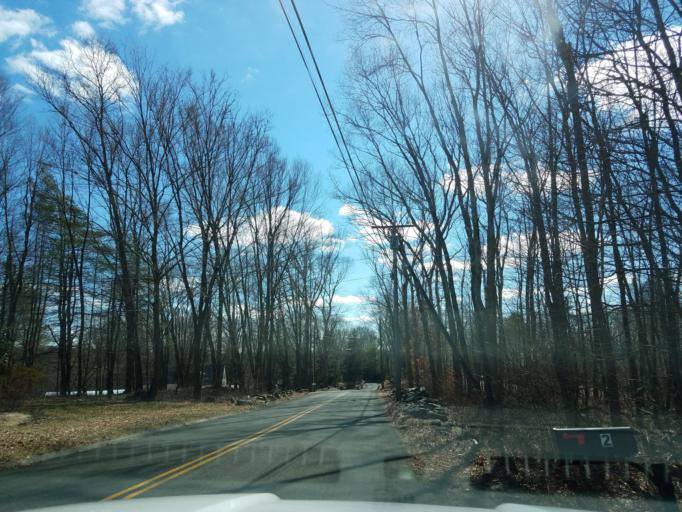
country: US
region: Connecticut
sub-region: Windham County
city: Thompson
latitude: 41.9735
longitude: -71.8784
